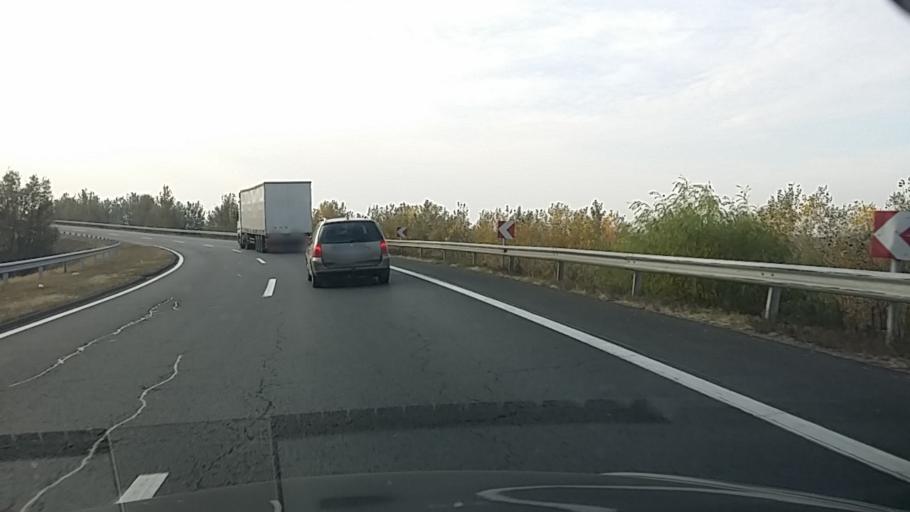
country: HU
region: Csongrad
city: Szatymaz
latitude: 46.3057
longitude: 20.0400
